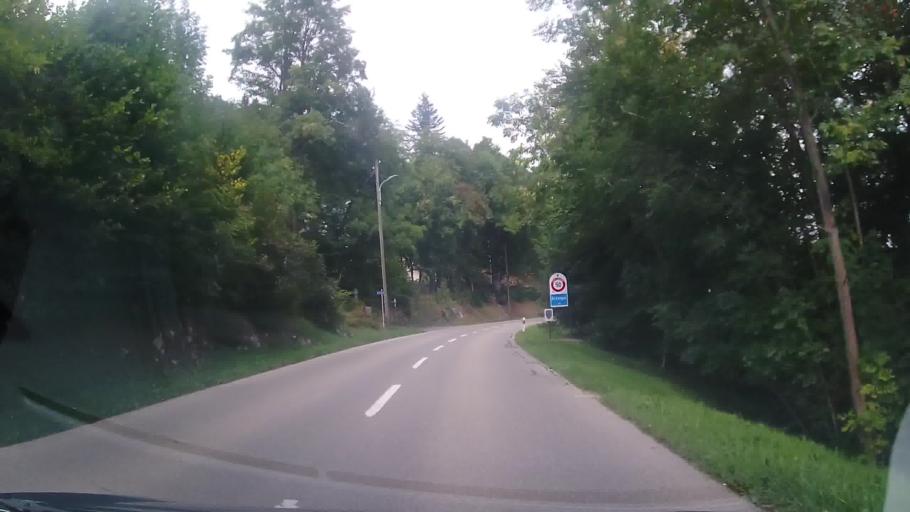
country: CH
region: Vaud
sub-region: Nyon District
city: Saint-Cergue
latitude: 46.4458
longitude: 6.1523
